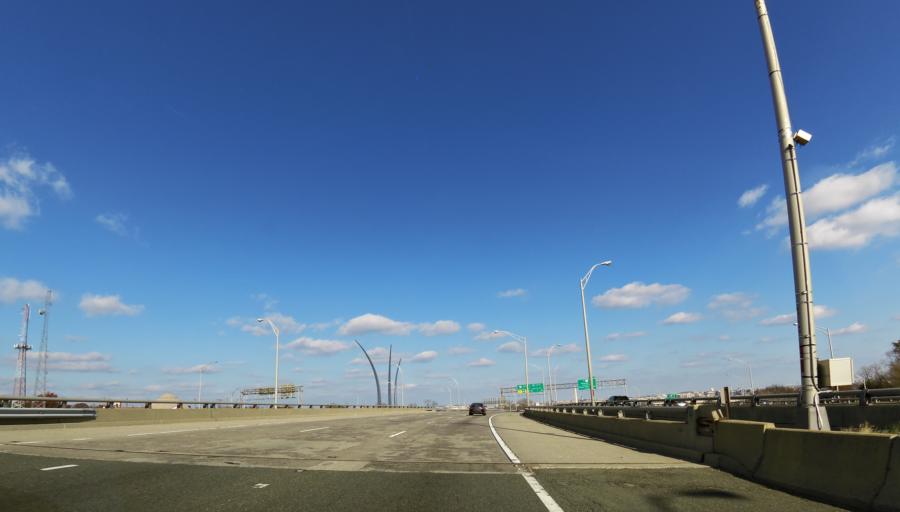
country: US
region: Virginia
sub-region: Arlington County
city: Arlington
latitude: 38.8646
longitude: -77.0685
